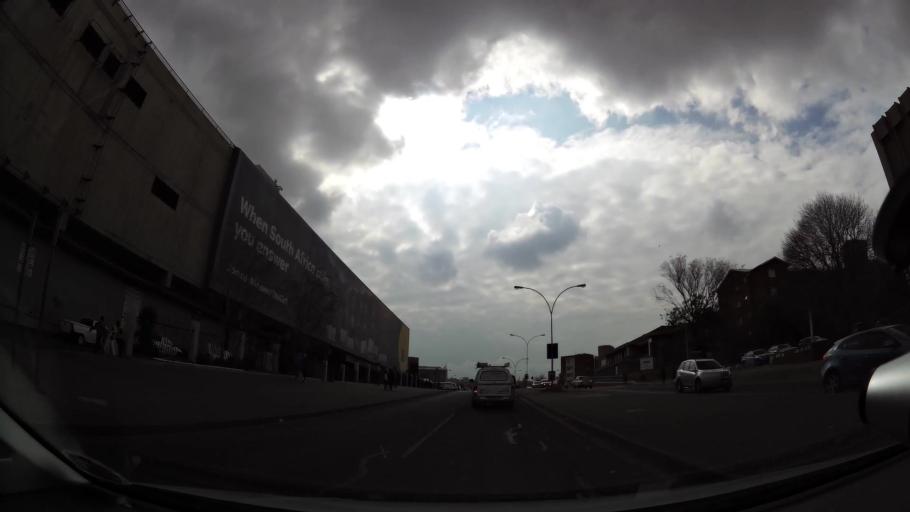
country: ZA
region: Orange Free State
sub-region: Mangaung Metropolitan Municipality
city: Bloemfontein
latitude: -29.1152
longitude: 26.2116
